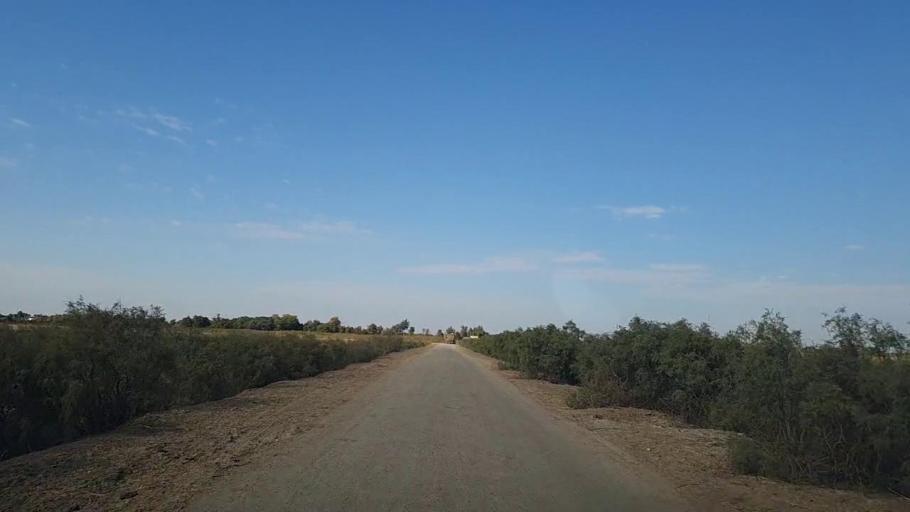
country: PK
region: Sindh
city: Khadro
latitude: 26.2995
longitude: 68.8202
